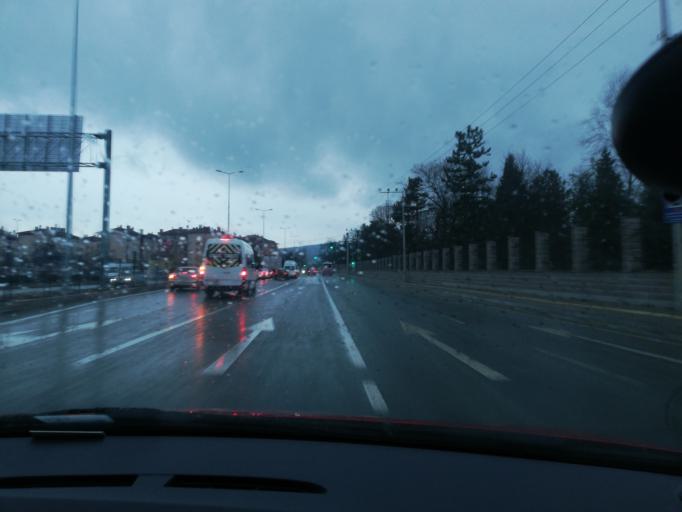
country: TR
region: Kastamonu
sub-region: Cide
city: Kastamonu
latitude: 41.4114
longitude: 33.7918
